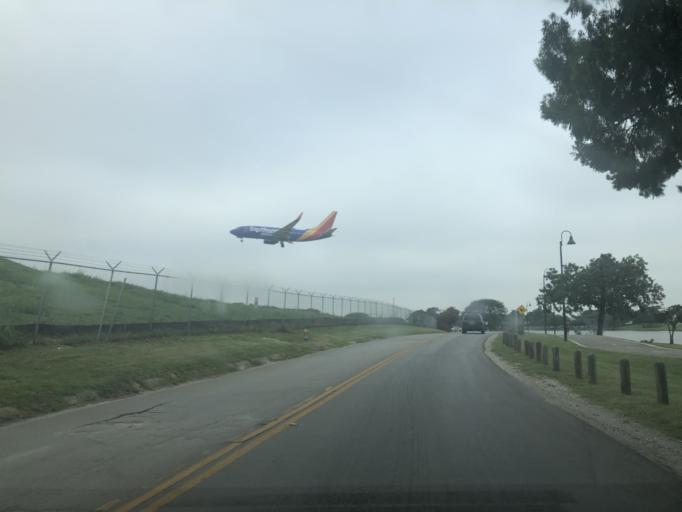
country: US
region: Texas
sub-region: Dallas County
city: University Park
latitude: 32.8590
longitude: -96.8560
